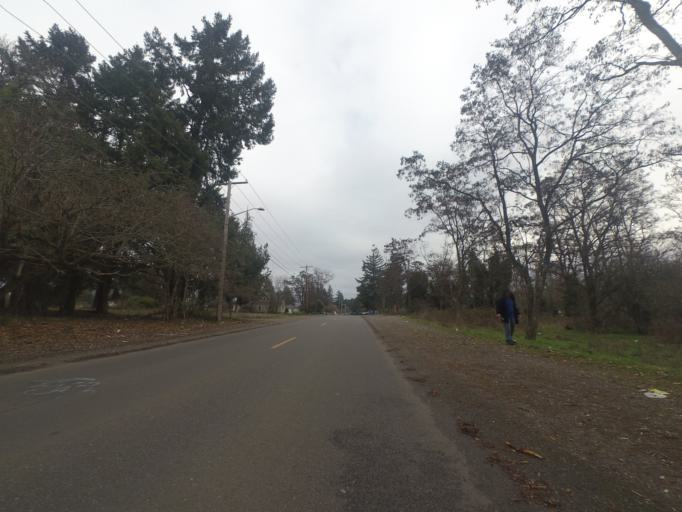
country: US
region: Washington
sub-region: Pierce County
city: McChord Air Force Base
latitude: 47.1248
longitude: -122.5332
